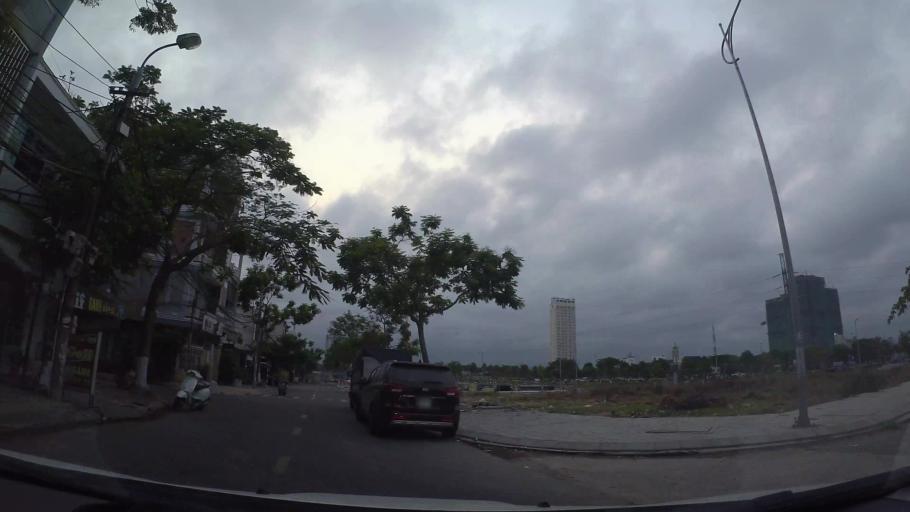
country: VN
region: Da Nang
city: Son Tra
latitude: 16.0507
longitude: 108.2370
